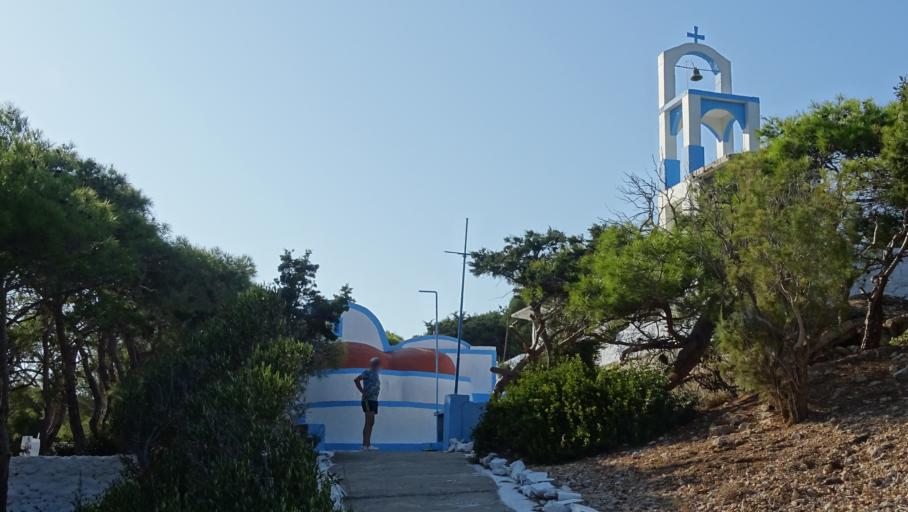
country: GR
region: South Aegean
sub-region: Nomos Dodekanisou
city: Kalymnos
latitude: 36.9139
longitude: 26.9408
